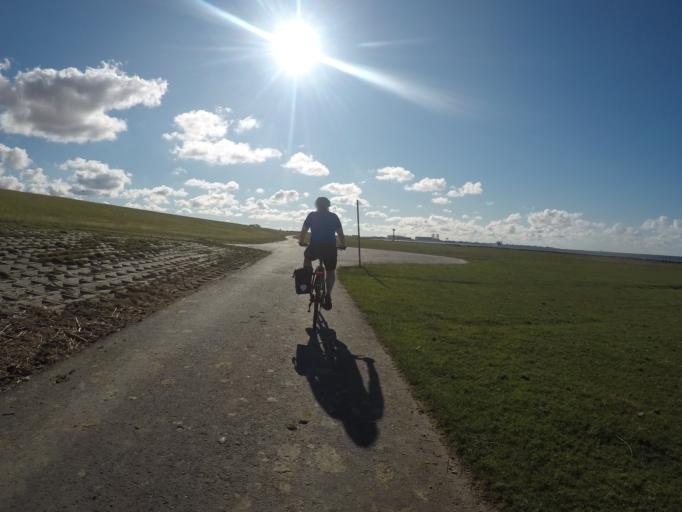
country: DE
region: Lower Saxony
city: Nordleda
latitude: 53.8319
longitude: 8.8051
